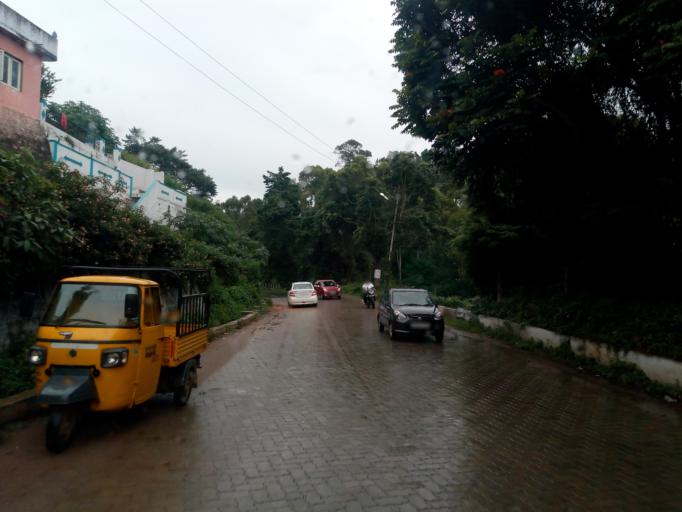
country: IN
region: Tamil Nadu
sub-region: Nilgiri
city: Wellington
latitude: 11.3484
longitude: 76.7877
